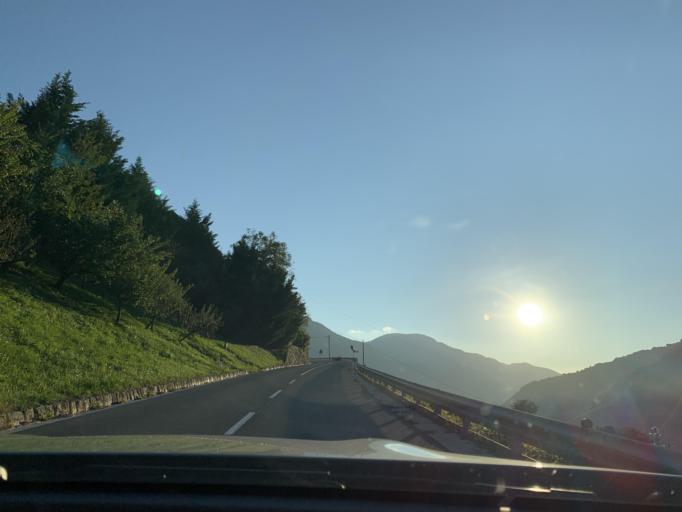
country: IT
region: Trentino-Alto Adige
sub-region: Bolzano
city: Collalbo
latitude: 46.5045
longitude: 11.4667
